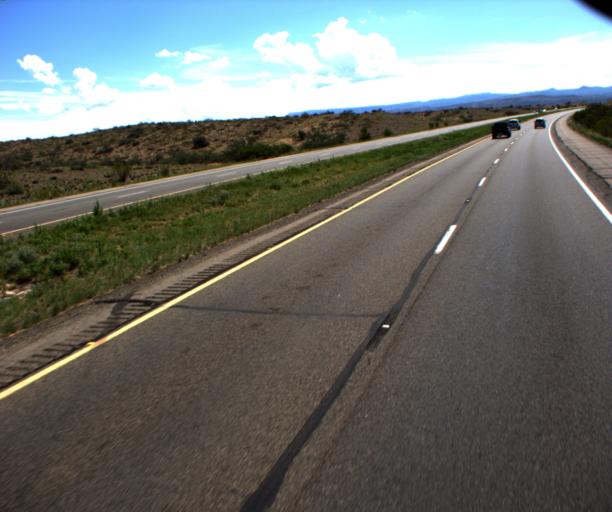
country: US
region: Arizona
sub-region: Yavapai County
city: Spring Valley
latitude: 34.3484
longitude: -112.1510
